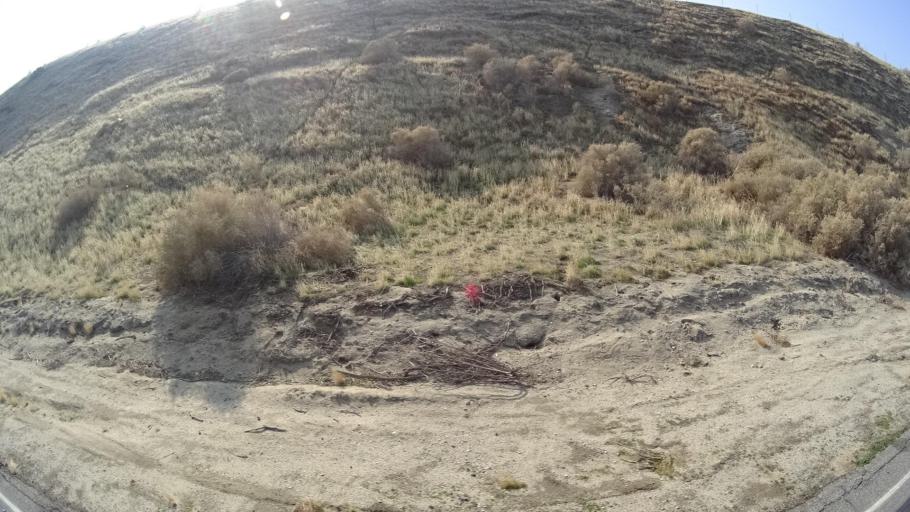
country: US
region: California
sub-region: Kern County
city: Buttonwillow
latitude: 35.2896
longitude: -119.3417
